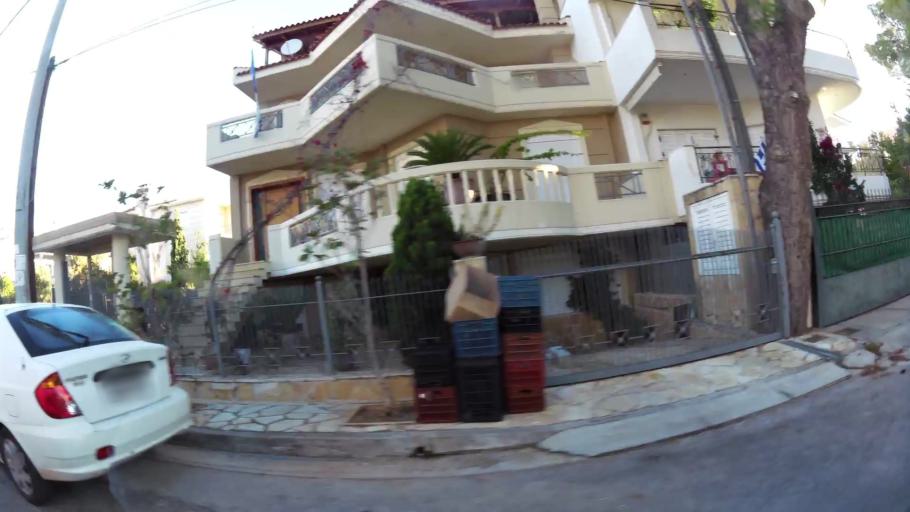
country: GR
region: Attica
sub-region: Nomarchia Anatolikis Attikis
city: Gerakas
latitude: 38.0316
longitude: 23.8522
